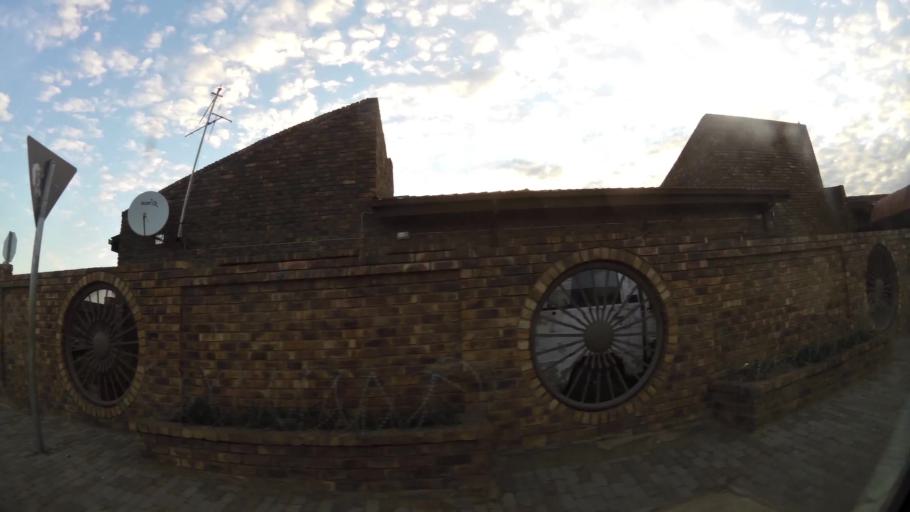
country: ZA
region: Gauteng
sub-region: City of Tshwane Metropolitan Municipality
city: Pretoria
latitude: -25.7121
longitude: 28.3439
